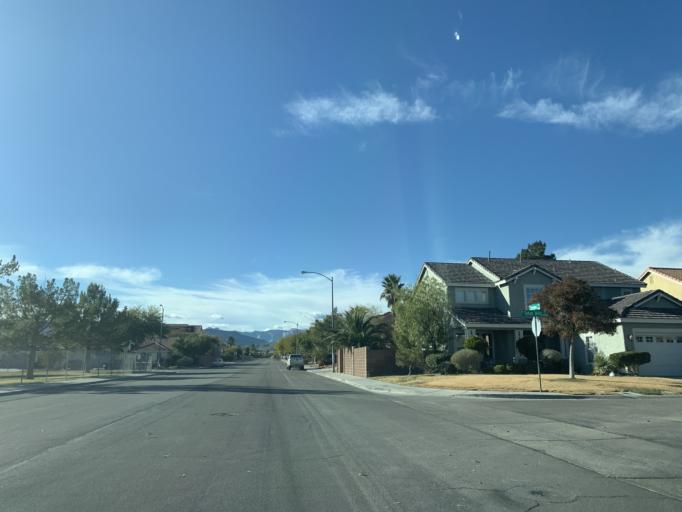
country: US
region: Nevada
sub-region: Clark County
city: Summerlin South
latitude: 36.1243
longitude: -115.3030
